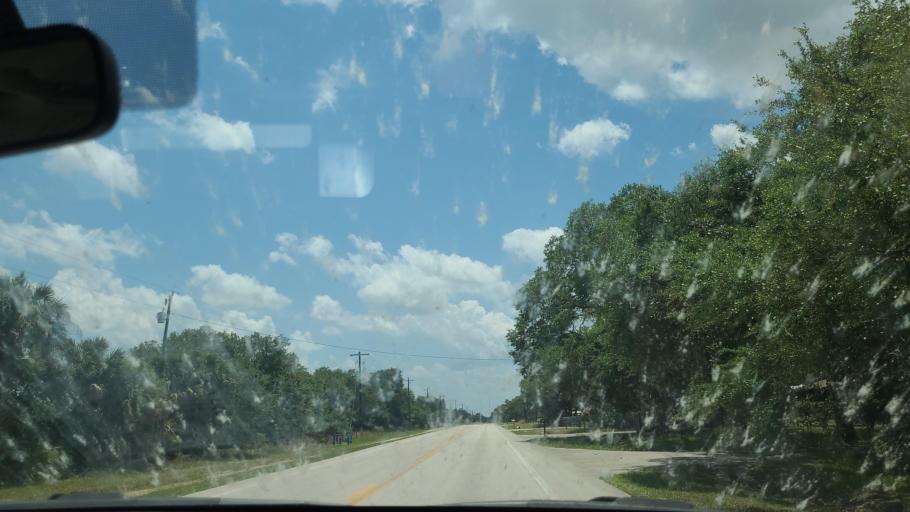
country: US
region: Florida
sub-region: Glades County
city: Buckhead Ridge
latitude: 27.0900
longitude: -81.0703
